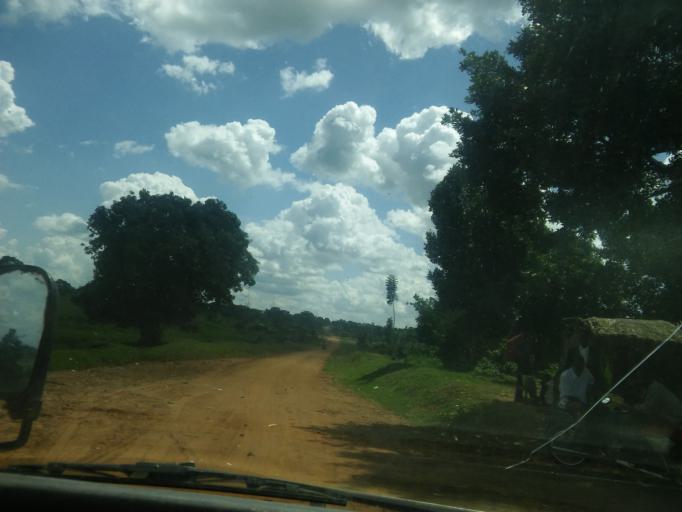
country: UG
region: Eastern Region
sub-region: Kibuku District
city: Kibuku
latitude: 1.1496
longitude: 33.8215
